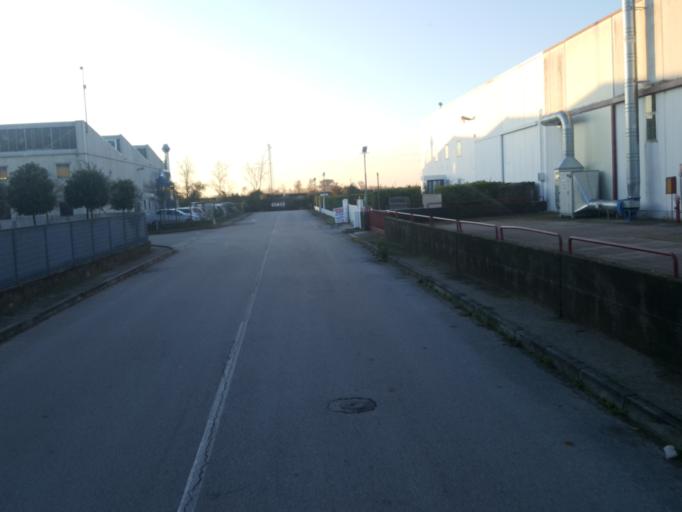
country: IT
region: Friuli Venezia Giulia
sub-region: Provincia di Pordenone
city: Orcenico Inferiore
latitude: 45.9480
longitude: 12.7721
